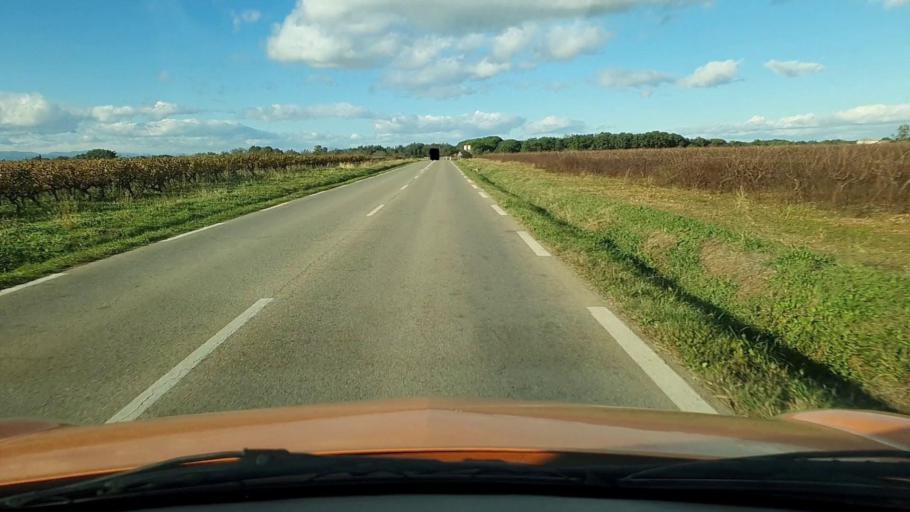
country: FR
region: Languedoc-Roussillon
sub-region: Departement du Gard
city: Vauvert
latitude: 43.6775
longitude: 4.2792
